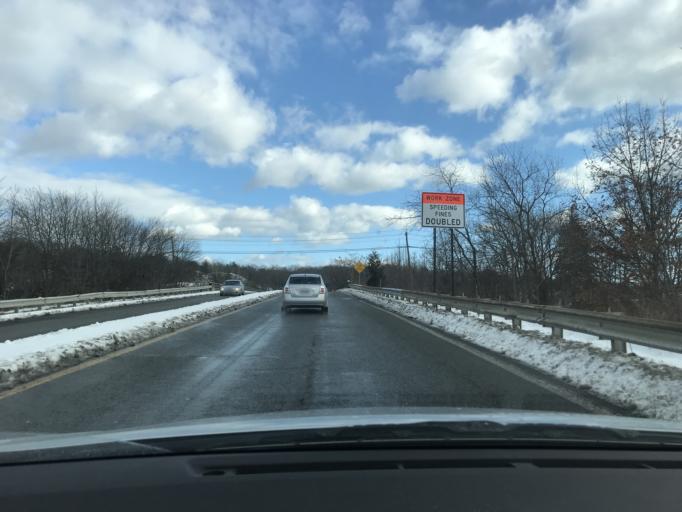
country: US
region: Massachusetts
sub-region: Essex County
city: Saugus
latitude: 42.4805
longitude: -71.0227
